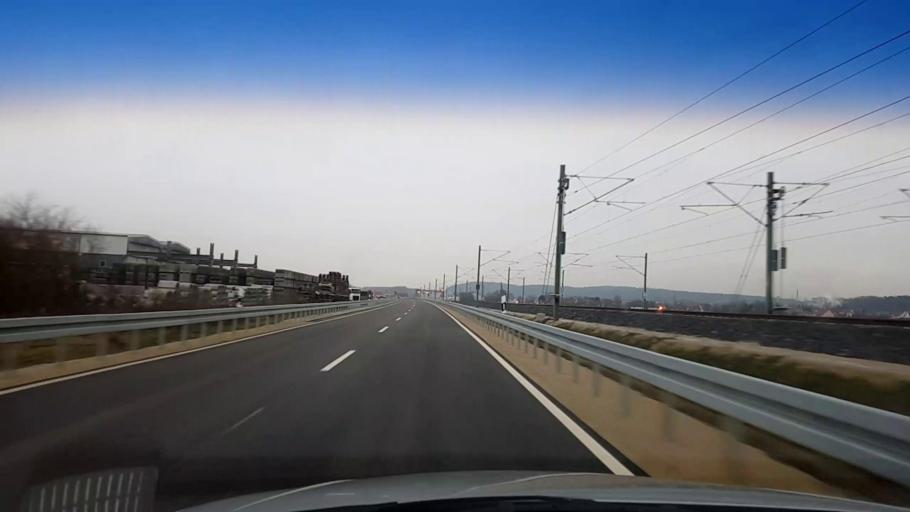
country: DE
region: Bavaria
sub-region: Upper Franconia
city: Zapfendorf
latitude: 50.0076
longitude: 10.9196
